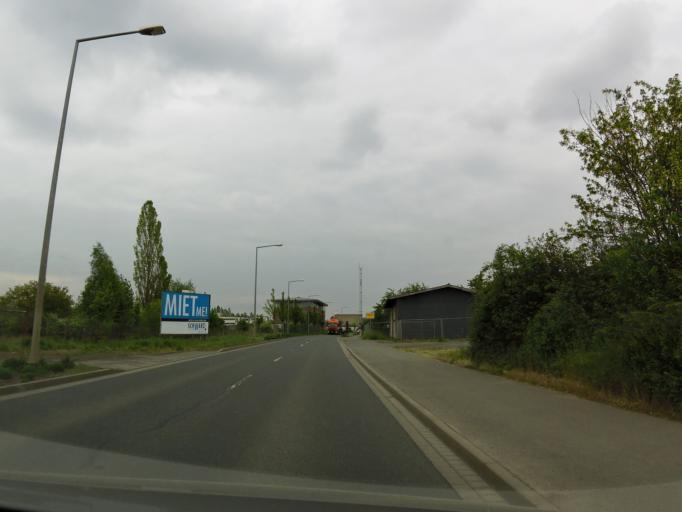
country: DE
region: Thuringia
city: Gotha
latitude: 50.9559
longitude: 10.7270
